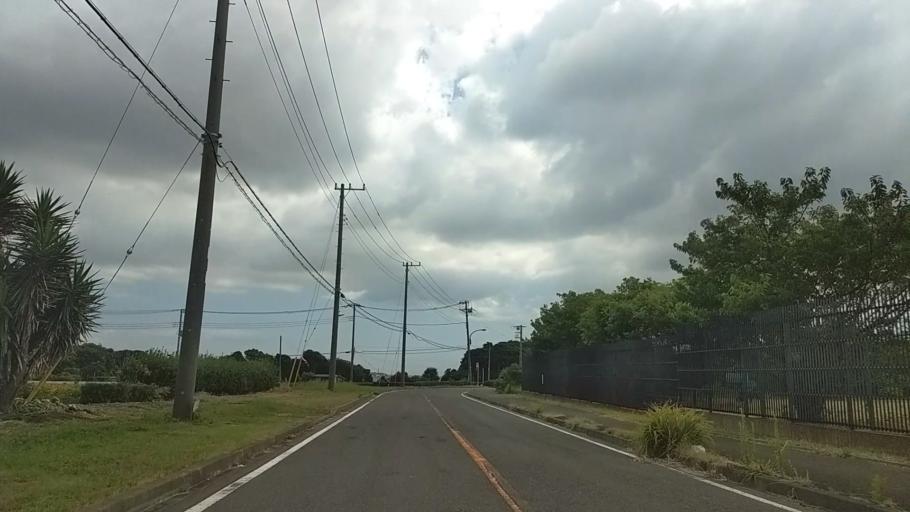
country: JP
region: Kanagawa
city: Miura
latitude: 35.1938
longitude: 139.6145
